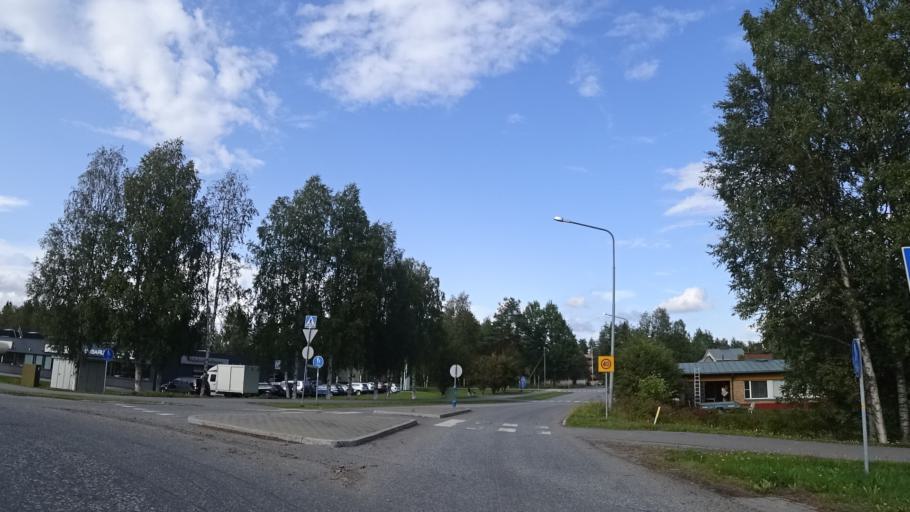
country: FI
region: North Karelia
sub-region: Pielisen Karjala
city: Lieksa
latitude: 63.3225
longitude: 30.0100
